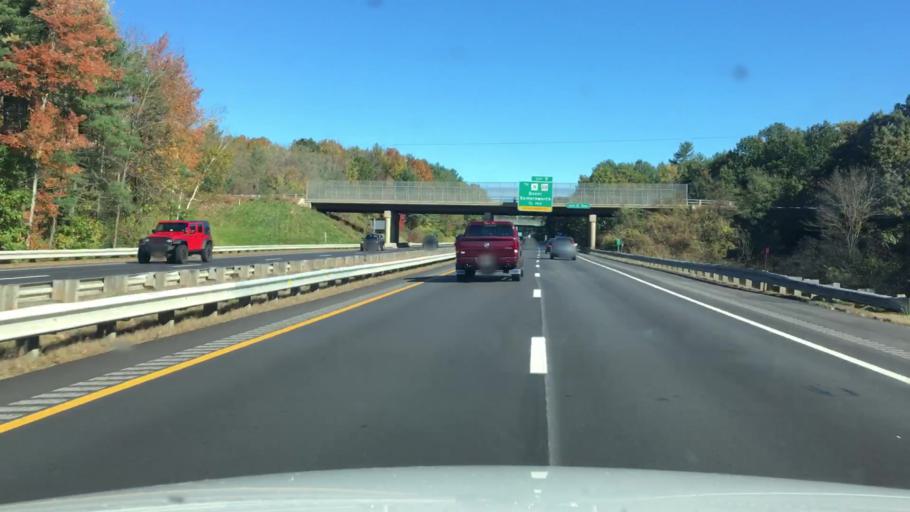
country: US
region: New Hampshire
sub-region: Strafford County
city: Dover
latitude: 43.2083
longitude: -70.8953
